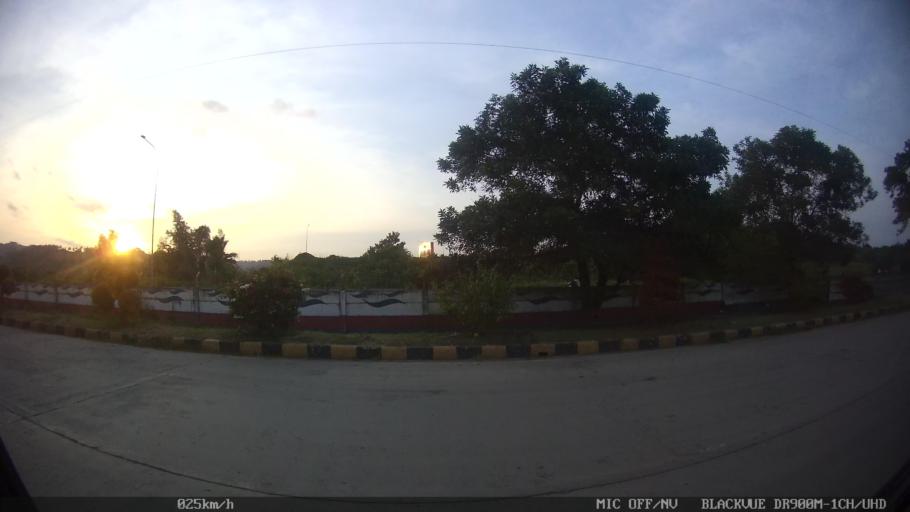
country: ID
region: Lampung
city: Penengahan
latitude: -5.8703
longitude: 105.7521
